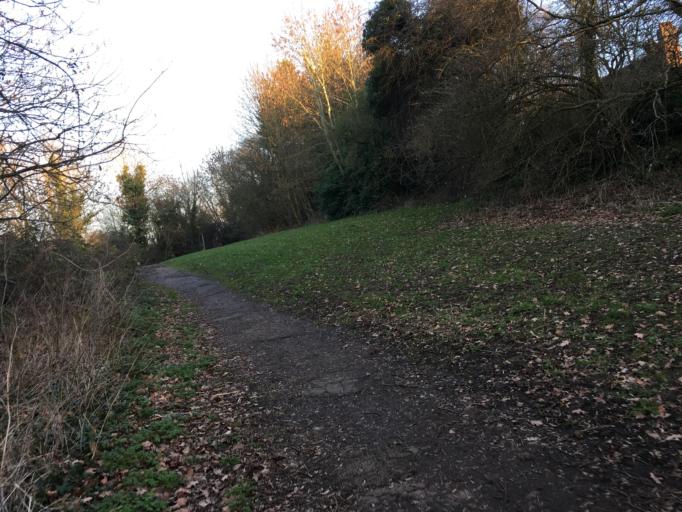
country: GB
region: England
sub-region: Greater London
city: Hendon
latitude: 51.5881
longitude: -0.1954
